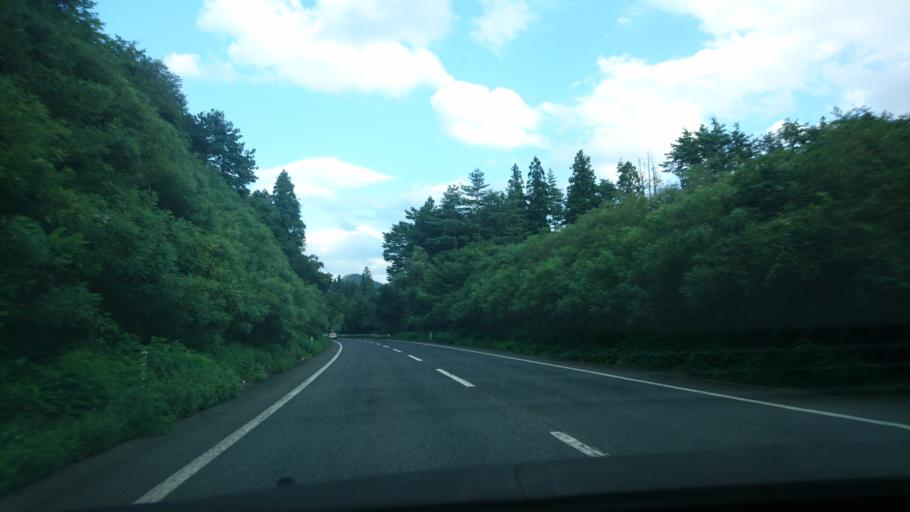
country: JP
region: Iwate
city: Mizusawa
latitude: 39.0365
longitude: 141.2508
